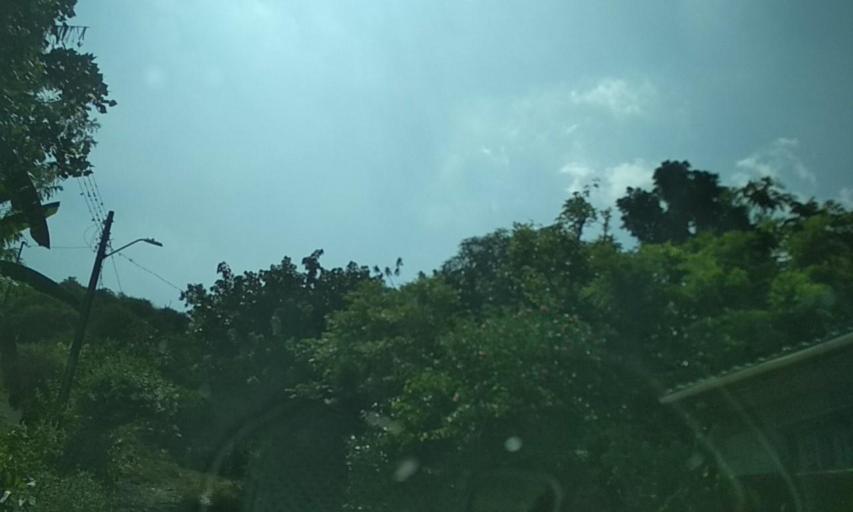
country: MX
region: Veracruz
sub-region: Atzalan
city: Colonias Pedernales
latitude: 20.0548
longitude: -97.0196
